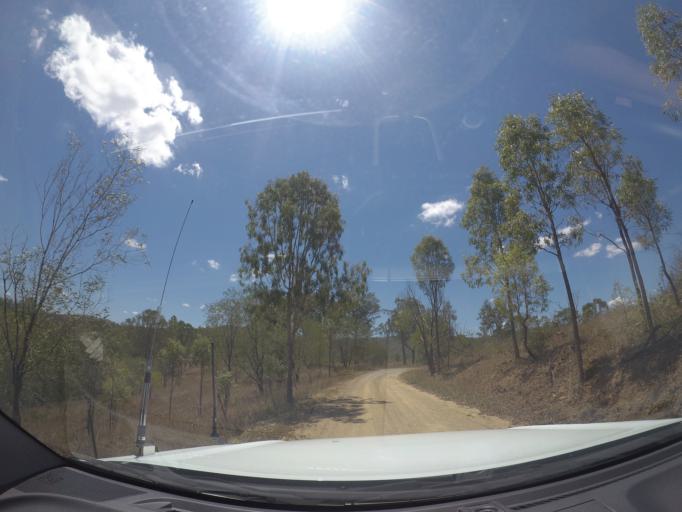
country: AU
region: Queensland
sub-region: Ipswich
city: Springfield Lakes
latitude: -27.8152
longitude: 152.8512
